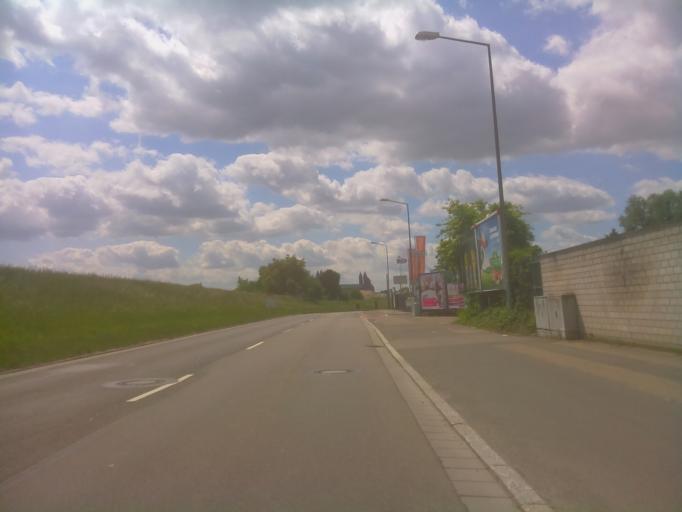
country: DE
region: Rheinland-Pfalz
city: Speyer
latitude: 49.3282
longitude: 8.4496
